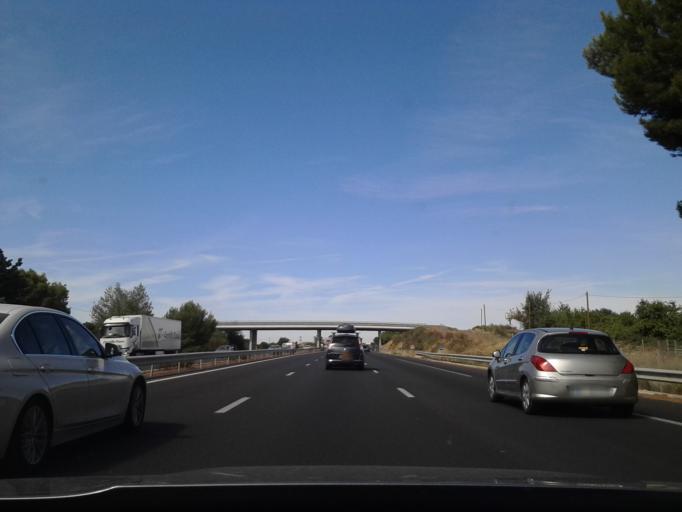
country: FR
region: Languedoc-Roussillon
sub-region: Departement de l'Herault
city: Pinet
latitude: 43.4102
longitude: 3.5056
